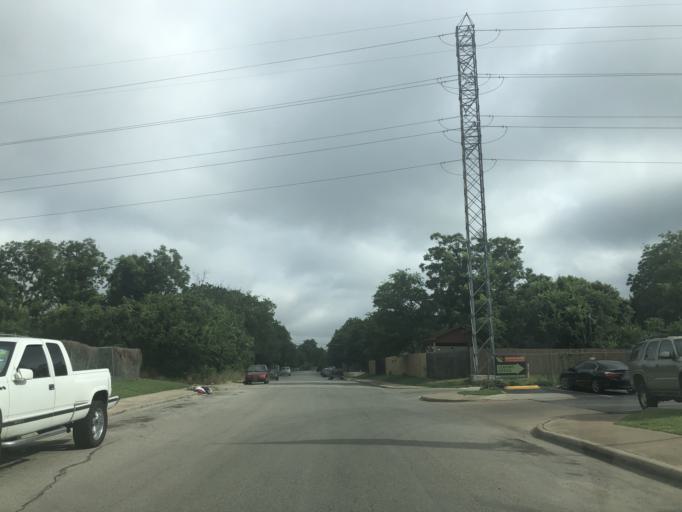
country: US
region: Texas
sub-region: Dallas County
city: University Park
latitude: 32.8655
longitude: -96.8583
